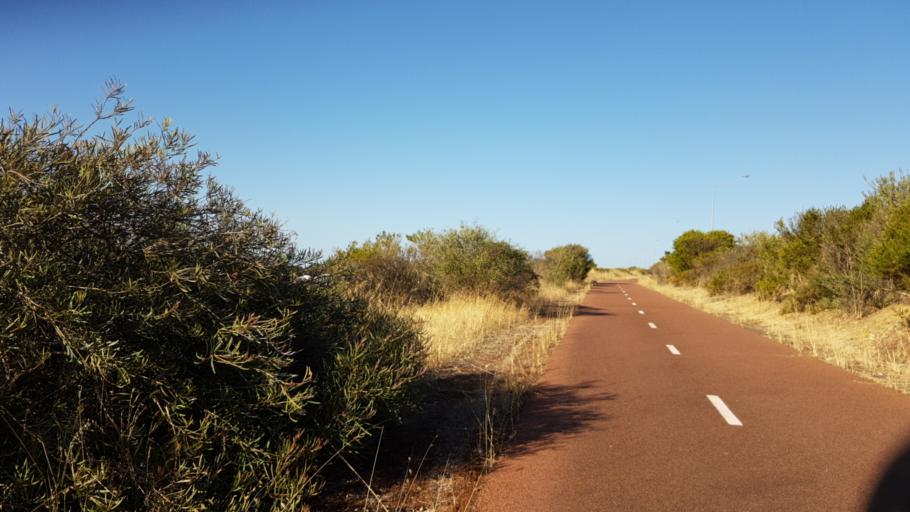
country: AU
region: Western Australia
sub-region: Kwinana
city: Wellard
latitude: -32.2730
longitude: 115.8433
